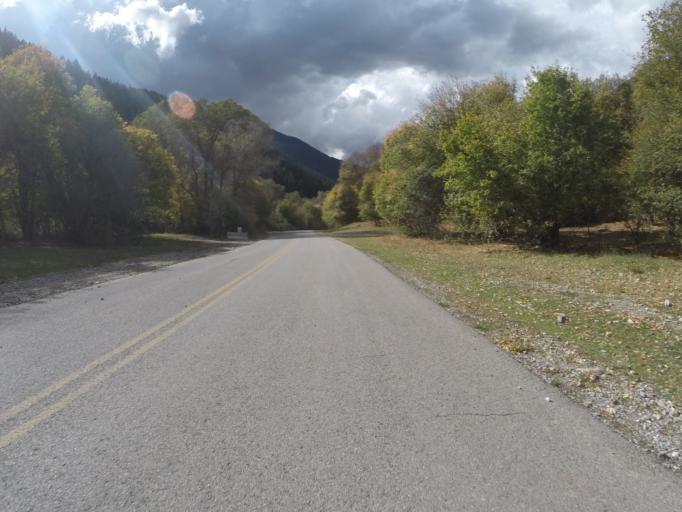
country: US
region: Utah
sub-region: Tooele County
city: Tooele
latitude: 40.4898
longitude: -112.1975
